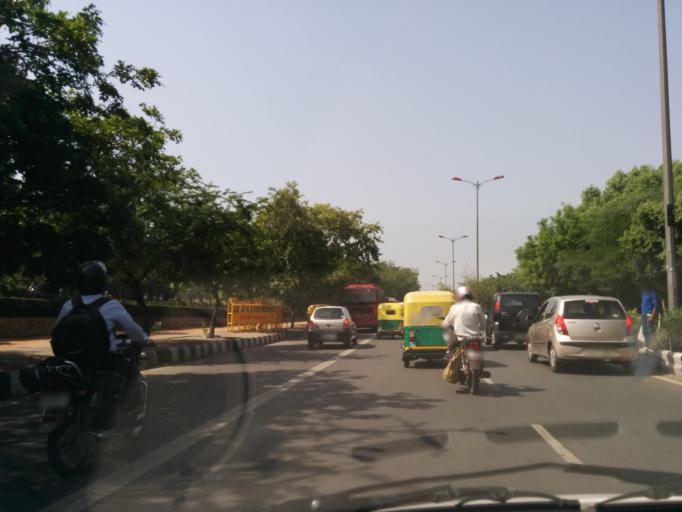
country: IN
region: NCT
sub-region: New Delhi
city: New Delhi
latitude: 28.5540
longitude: 77.2054
